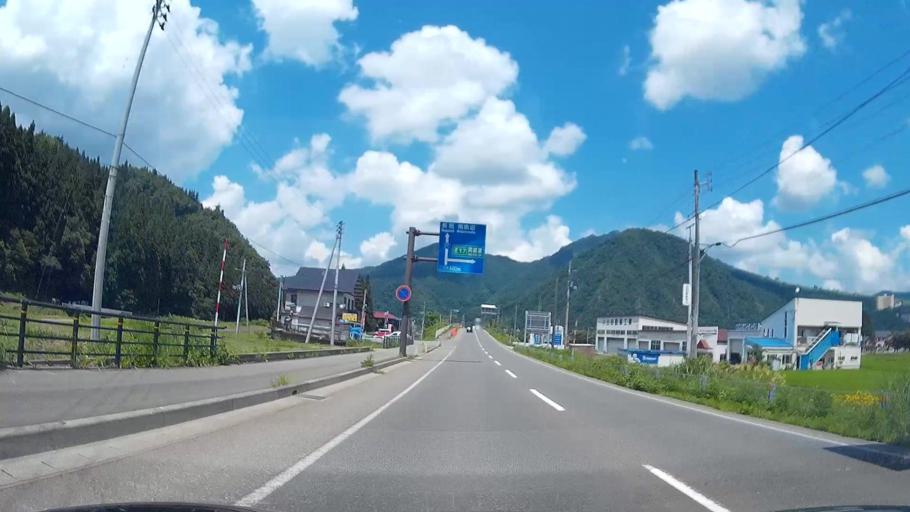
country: JP
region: Niigata
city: Shiozawa
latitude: 36.9253
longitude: 138.8240
